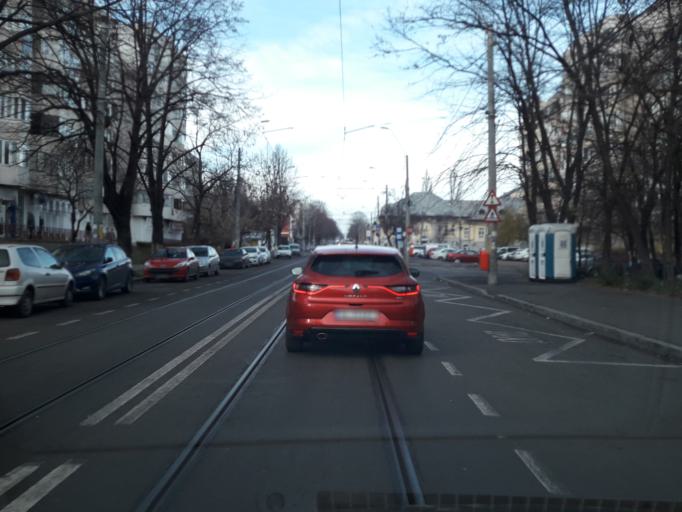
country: RO
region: Galati
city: Galati
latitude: 45.4424
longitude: 28.0475
